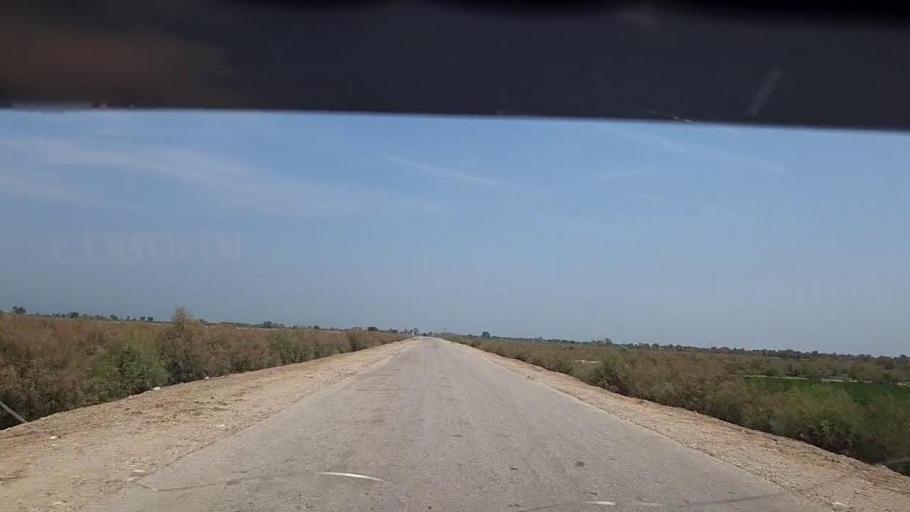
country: PK
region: Sindh
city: Thul
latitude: 28.2072
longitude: 68.8134
